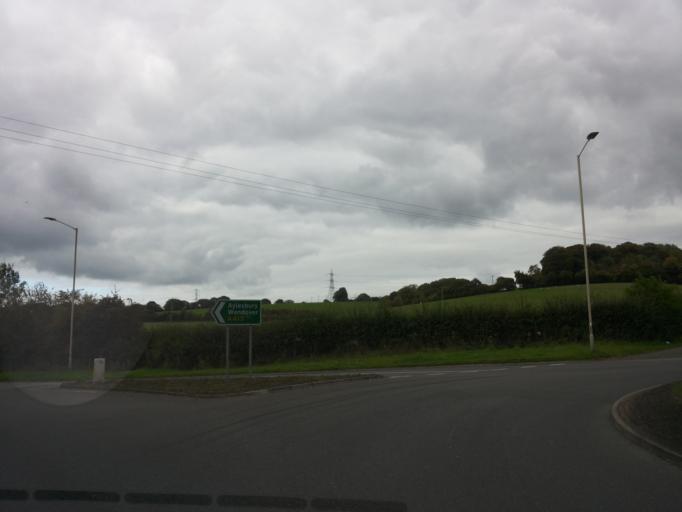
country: GB
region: England
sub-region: Buckinghamshire
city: Great Missenden
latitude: 51.7057
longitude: -0.7044
